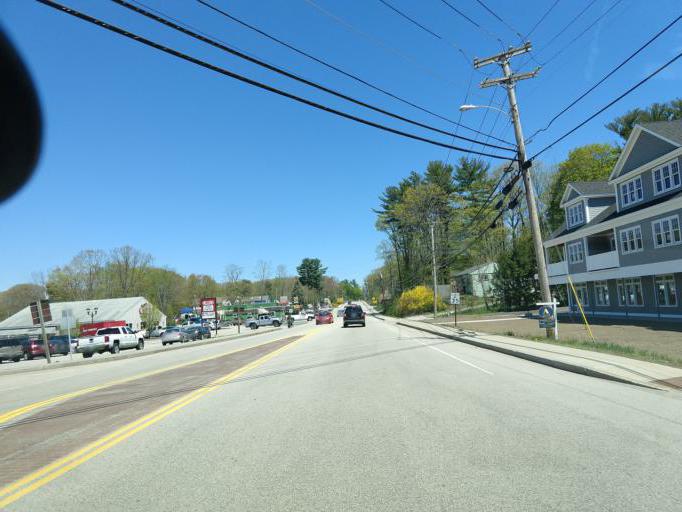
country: US
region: Maine
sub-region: York County
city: Kittery
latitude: 43.0884
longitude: -70.7493
